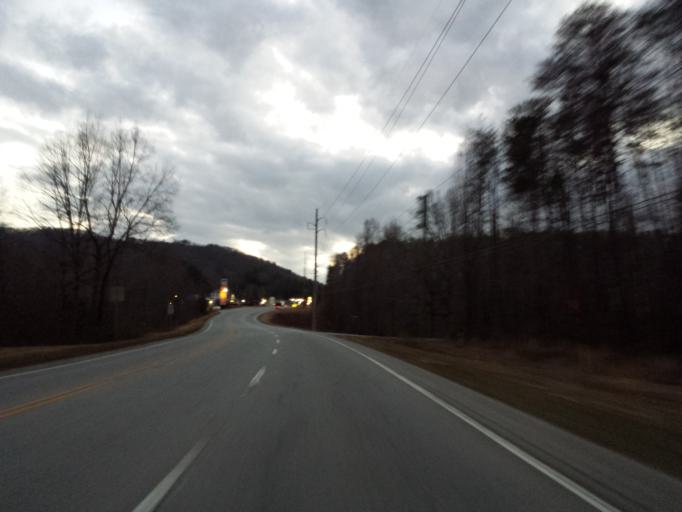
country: US
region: Georgia
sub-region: White County
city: Cleveland
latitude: 34.6654
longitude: -83.7179
